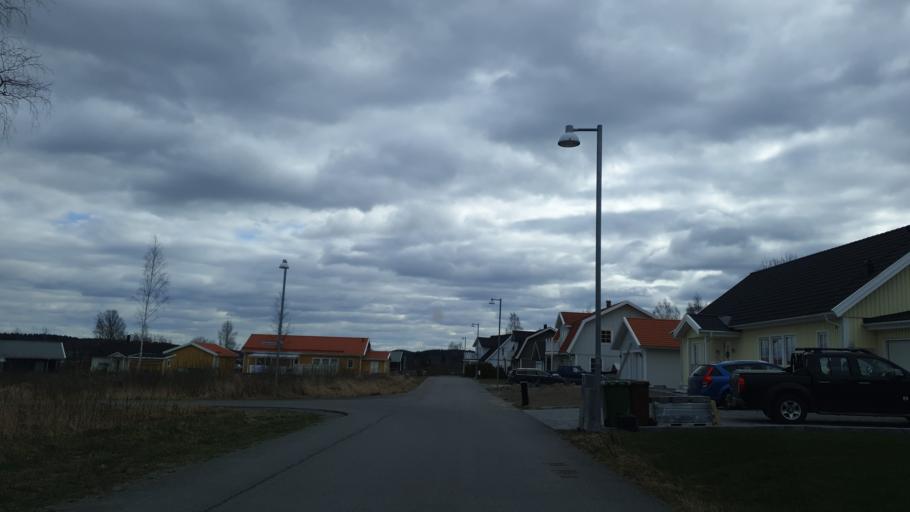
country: SE
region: OErebro
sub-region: Nora Kommun
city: Nora
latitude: 59.5317
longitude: 15.0379
